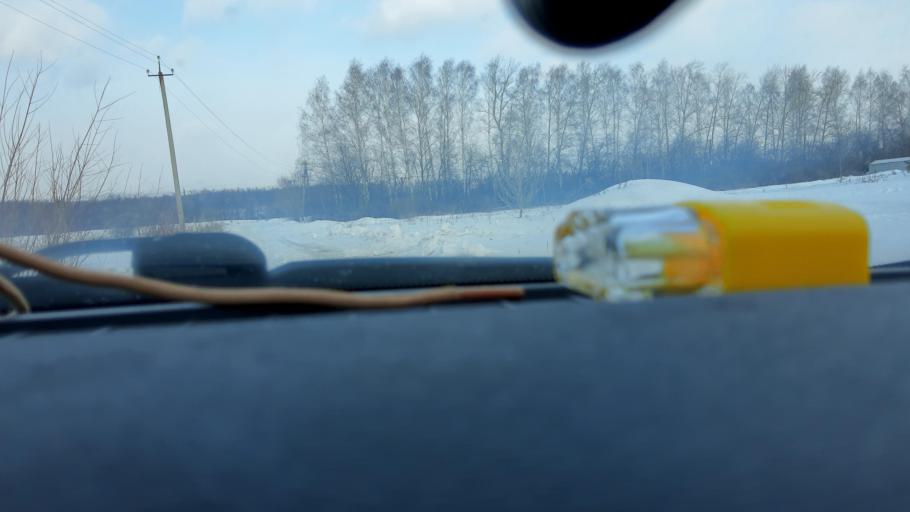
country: RU
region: Bashkortostan
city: Kabakovo
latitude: 54.6347
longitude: 56.0633
